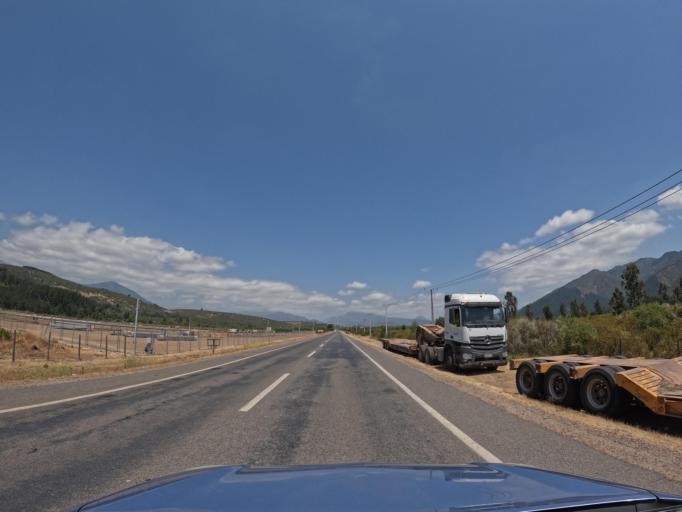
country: CL
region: Maule
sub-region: Provincia de Curico
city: Molina
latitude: -35.1671
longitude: -71.1304
